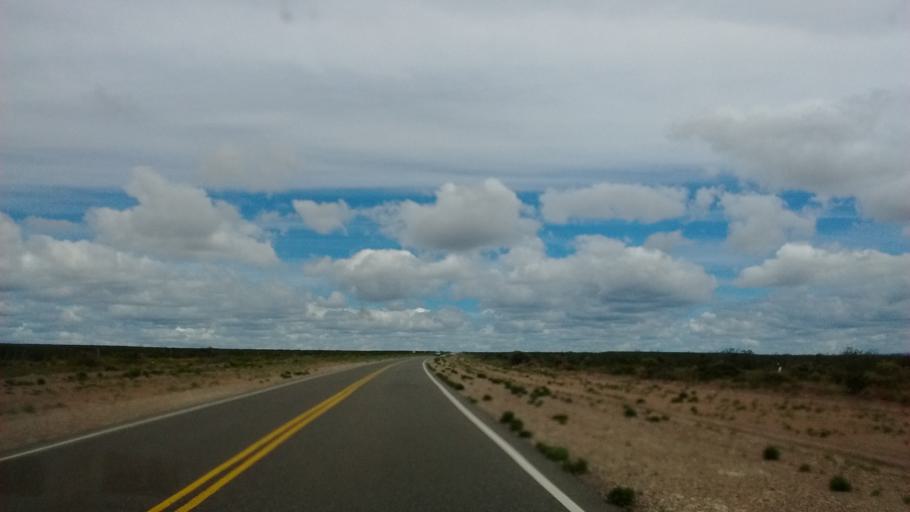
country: AR
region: Neuquen
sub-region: Departamento de Picun Leufu
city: Picun Leufu
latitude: -39.7479
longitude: -69.6175
